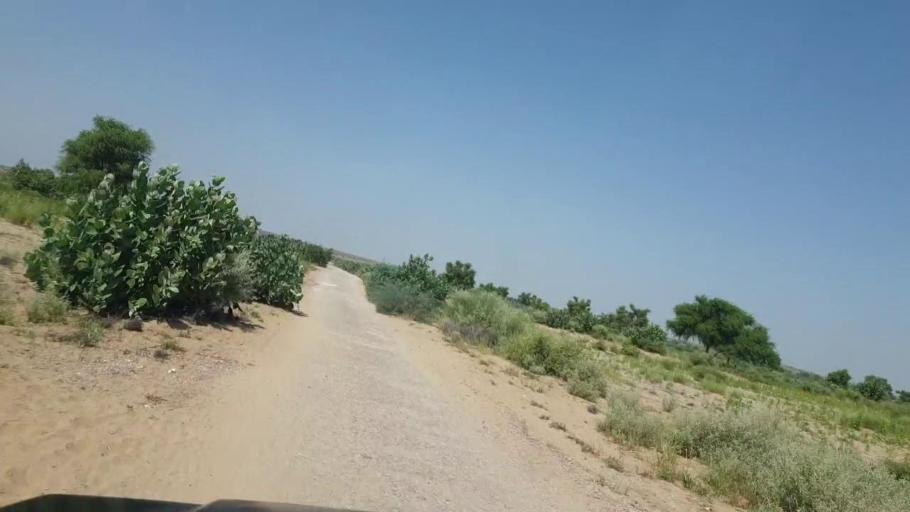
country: PK
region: Sindh
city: Chor
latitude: 25.3653
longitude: 70.3237
